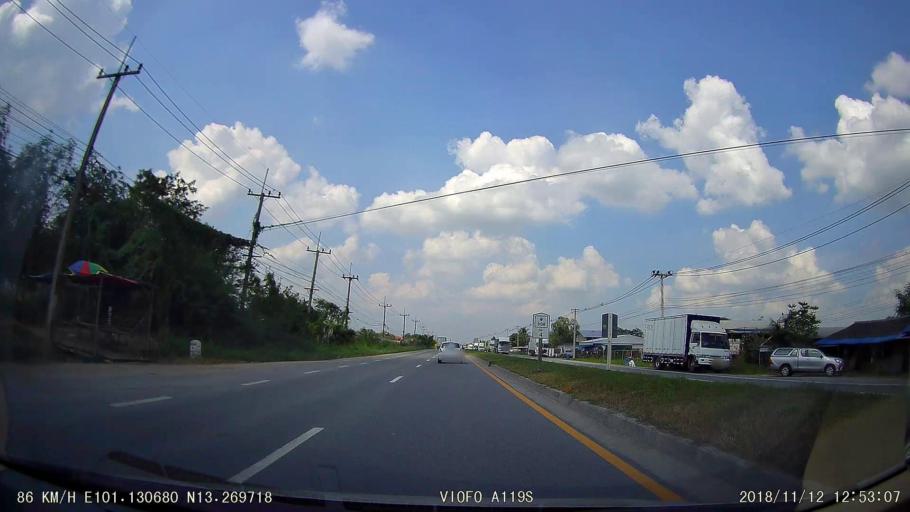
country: TH
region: Chon Buri
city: Ban Bueng
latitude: 13.2699
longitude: 101.1306
